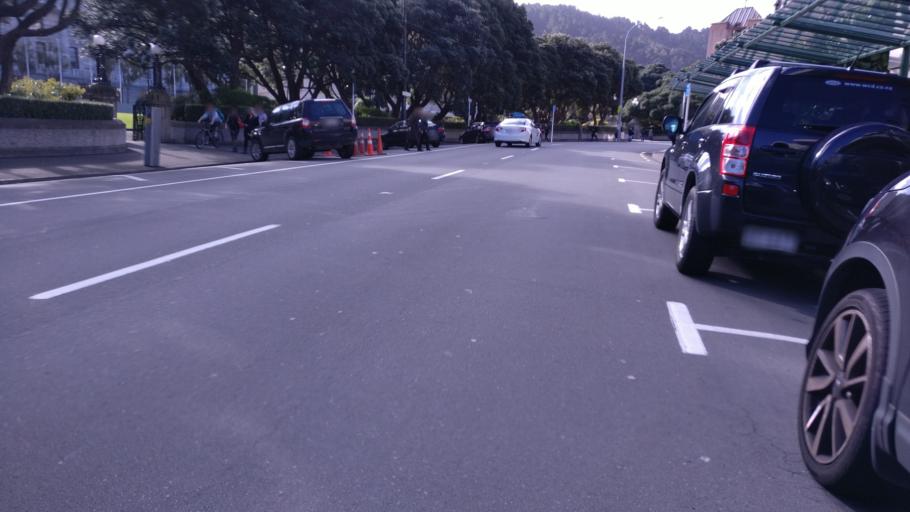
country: NZ
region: Wellington
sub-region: Wellington City
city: Wellington
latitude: -41.2781
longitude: 174.7780
